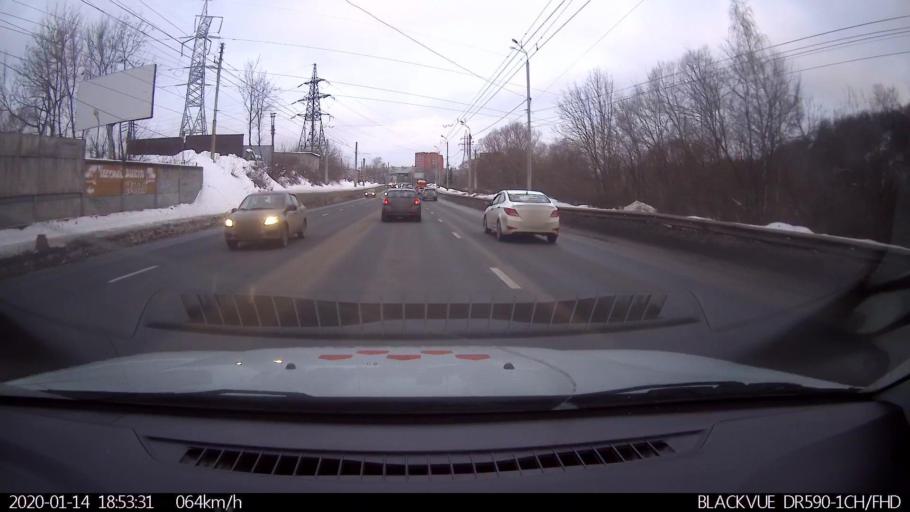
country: RU
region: Nizjnij Novgorod
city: Afonino
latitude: 56.3023
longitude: 44.0536
